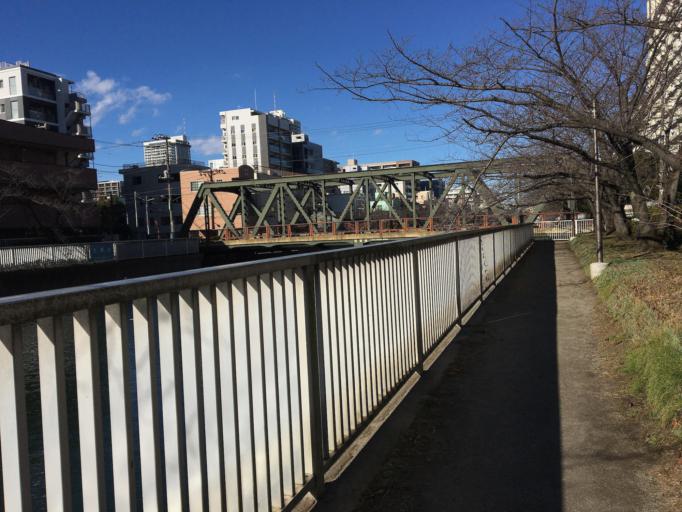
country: JP
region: Tokyo
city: Urayasu
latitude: 35.6778
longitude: 139.8108
